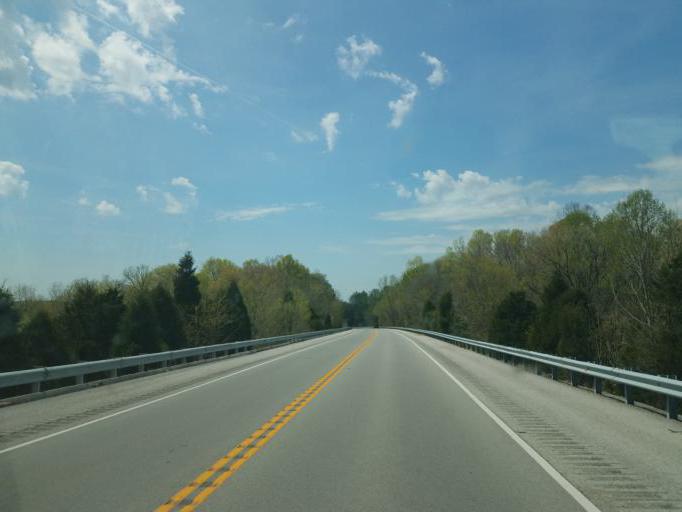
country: US
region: Kentucky
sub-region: Warren County
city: Bowling Green
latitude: 37.0922
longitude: -86.4444
